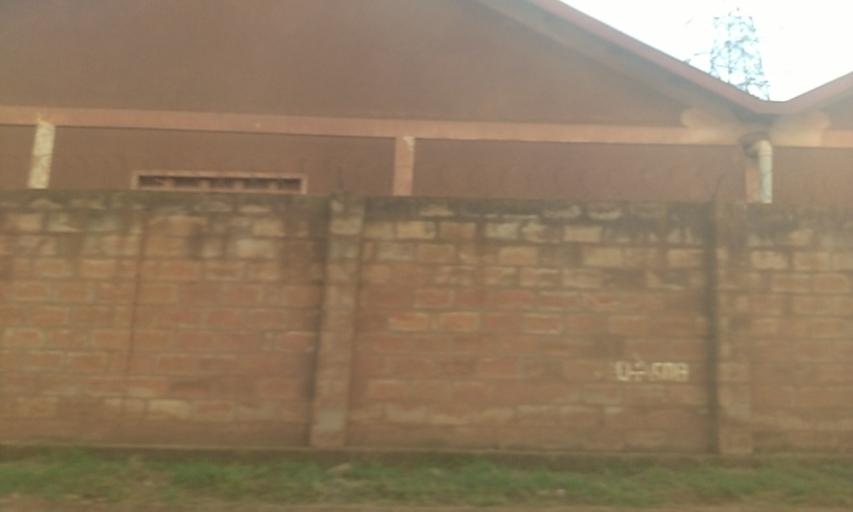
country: UG
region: Central Region
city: Kampala Central Division
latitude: 0.2980
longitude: 32.5287
